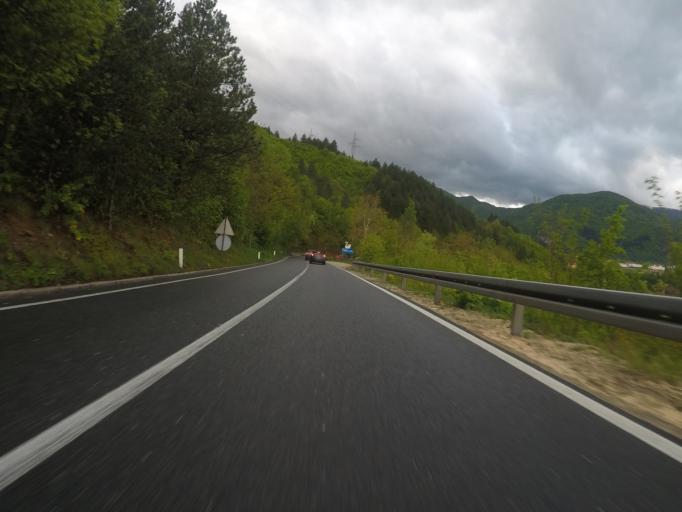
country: BA
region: Federation of Bosnia and Herzegovina
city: Jablanica
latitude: 43.6497
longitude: 17.7542
